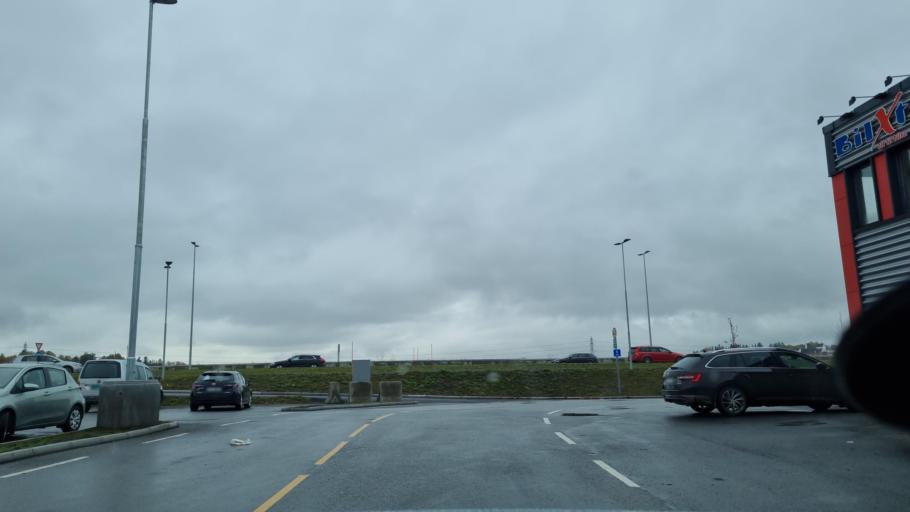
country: NO
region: Hedmark
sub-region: Hamar
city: Hamar
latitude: 60.7979
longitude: 11.1098
